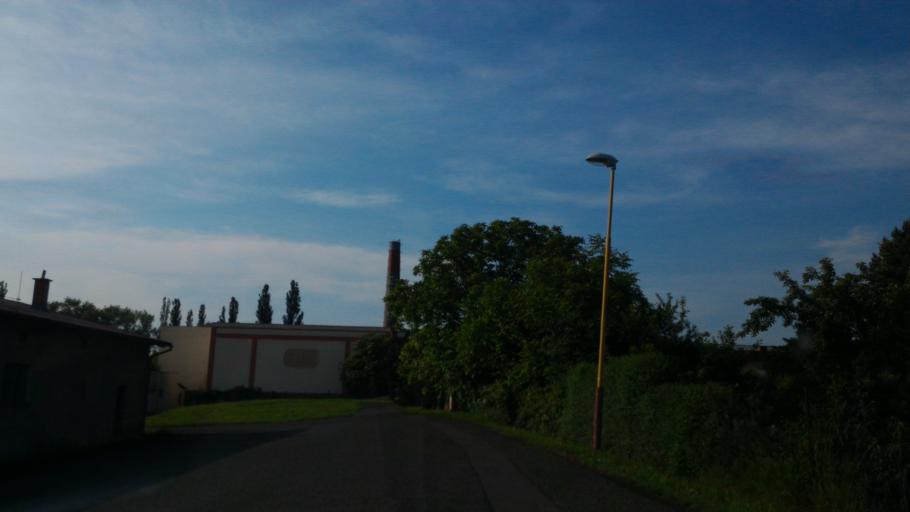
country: CZ
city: Hradek nad Nisou
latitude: 50.8572
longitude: 14.8436
